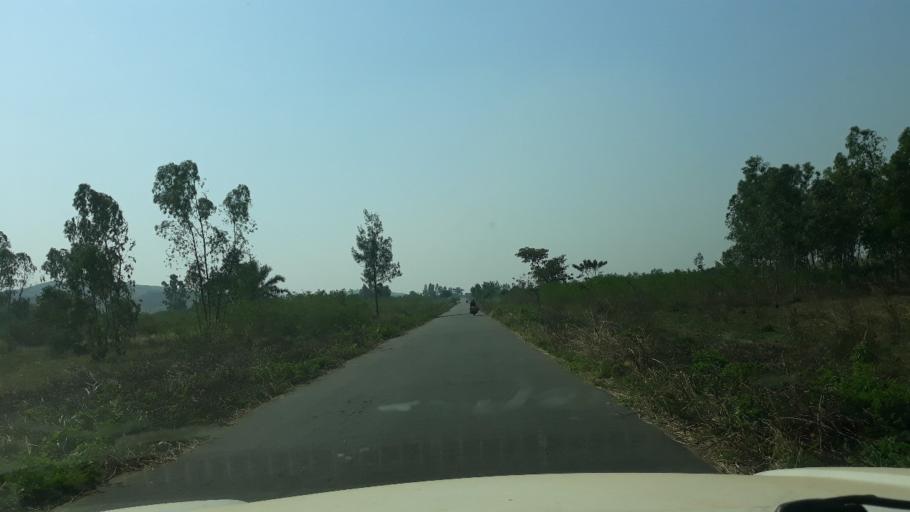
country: CD
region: South Kivu
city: Uvira
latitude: -3.2161
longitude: 29.1648
